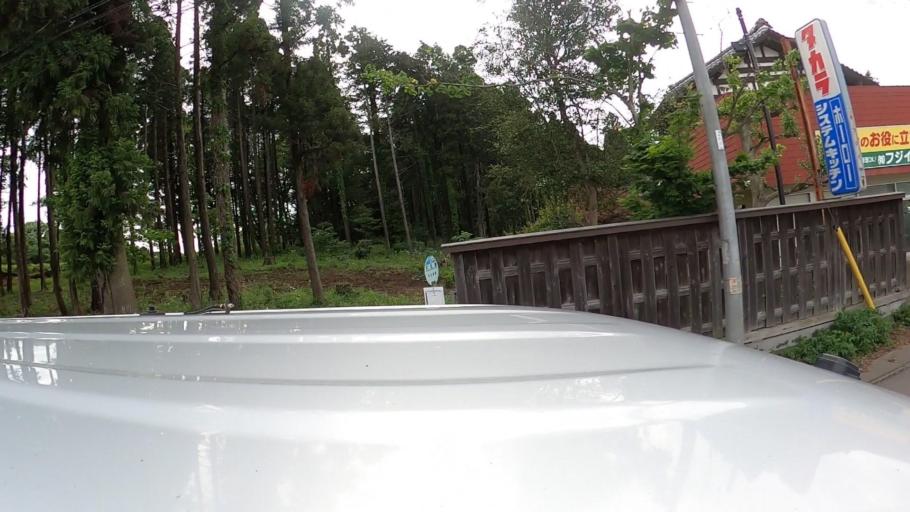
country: JP
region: Ibaraki
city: Ami
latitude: 35.9646
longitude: 140.2288
